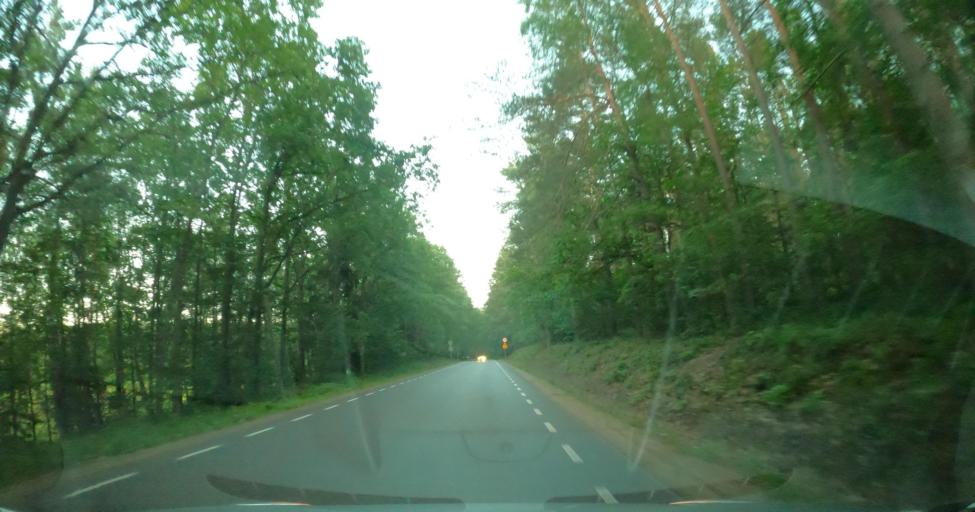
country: PL
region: Pomeranian Voivodeship
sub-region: Powiat leborski
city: Lebork
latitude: 54.5198
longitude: 17.7846
